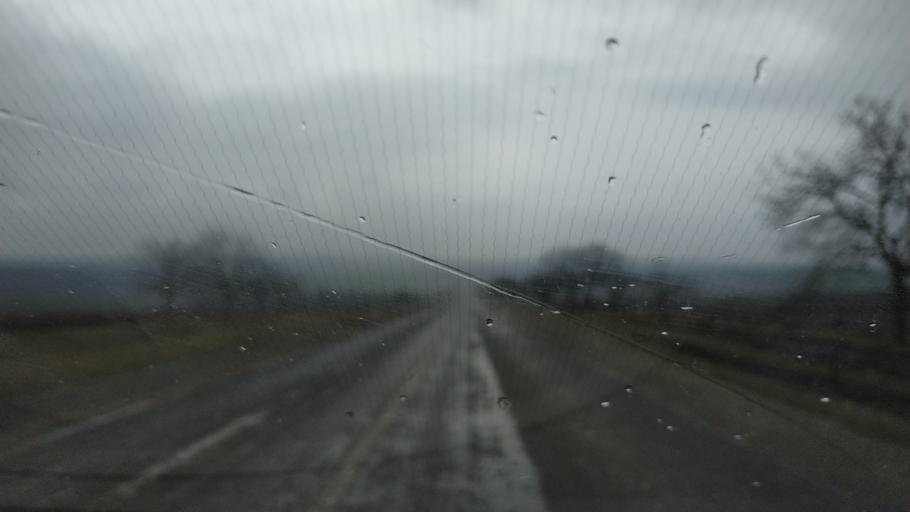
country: MD
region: Gagauzia
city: Comrat
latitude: 46.3084
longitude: 28.6067
